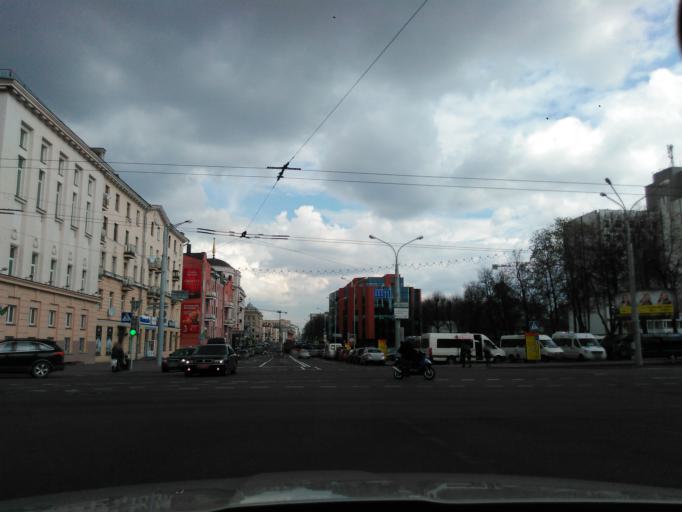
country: BY
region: Minsk
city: Minsk
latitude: 53.8939
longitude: 27.5531
